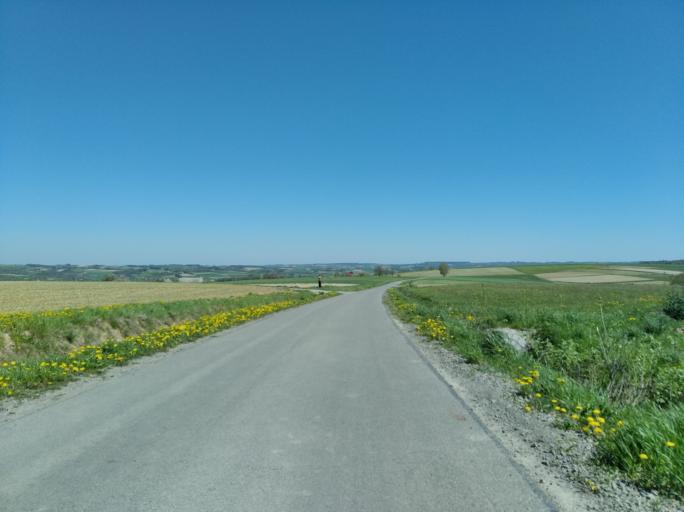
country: PL
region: Subcarpathian Voivodeship
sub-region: Powiat ropczycko-sedziszowski
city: Wielopole Skrzynskie
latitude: 49.9052
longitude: 21.5509
